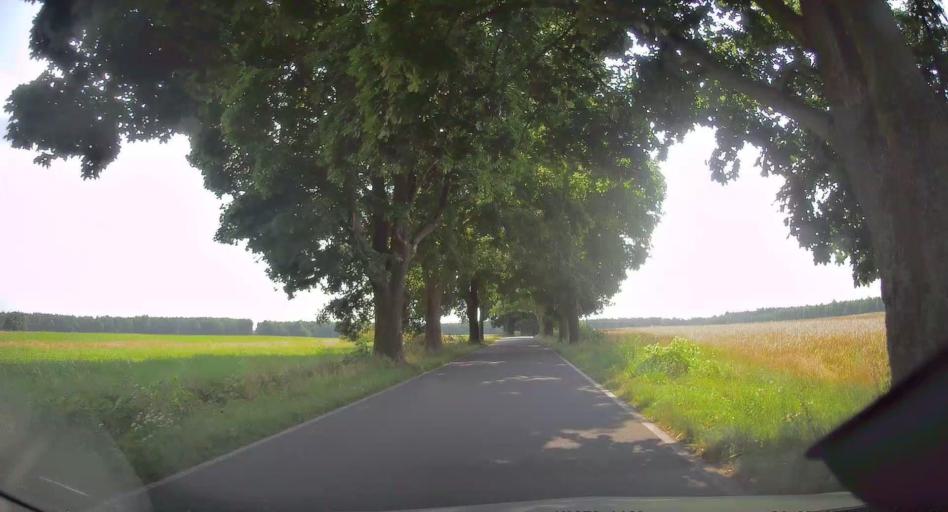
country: PL
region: Lodz Voivodeship
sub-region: Powiat tomaszowski
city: Lubochnia
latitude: 51.5646
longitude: 20.1184
